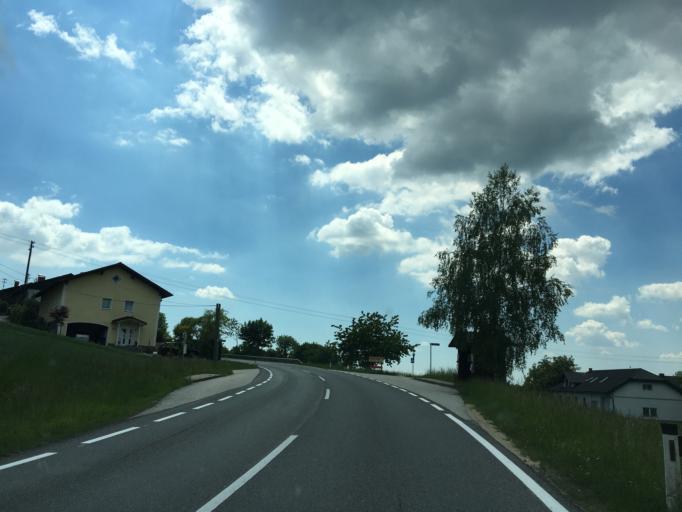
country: AT
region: Upper Austria
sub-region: Politischer Bezirk Urfahr-Umgebung
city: Engerwitzdorf
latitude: 48.3794
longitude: 14.5436
